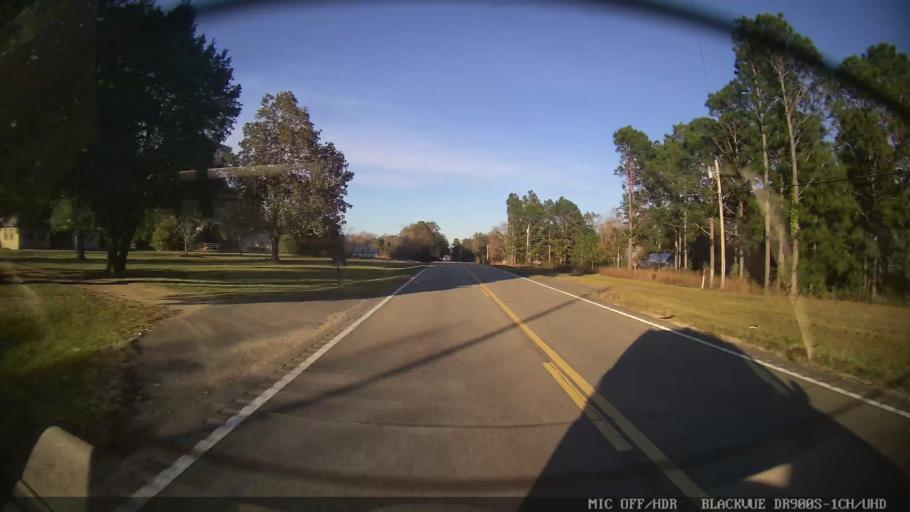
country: US
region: Mississippi
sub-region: Lamar County
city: Lumberton
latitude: 31.0403
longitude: -89.4385
